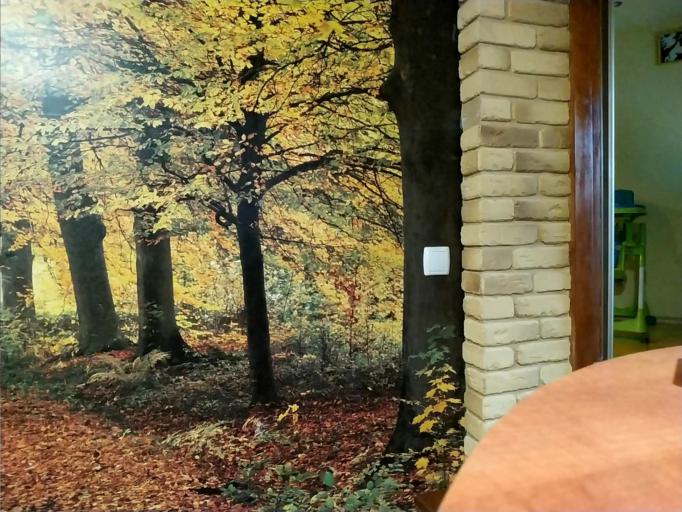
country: BY
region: Minsk
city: Il'ya
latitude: 54.4227
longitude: 27.4821
